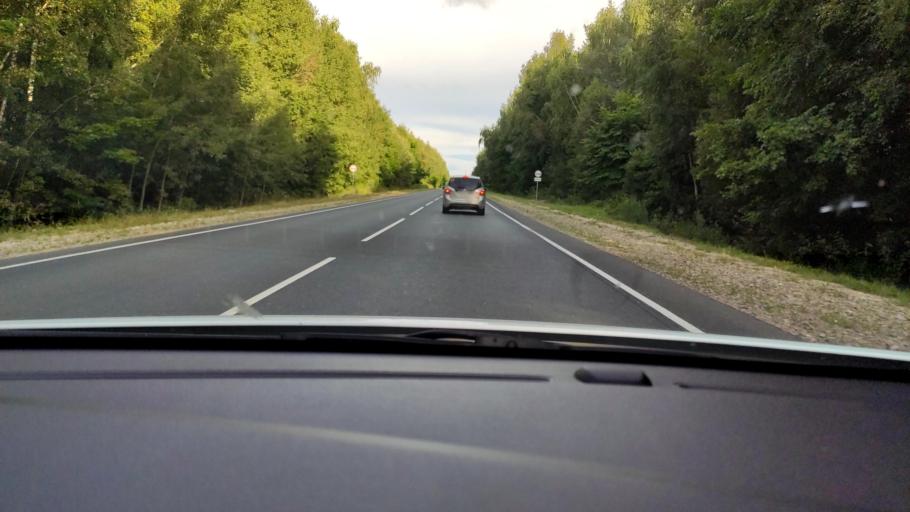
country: RU
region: Mariy-El
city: Krasnogorskiy
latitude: 56.1858
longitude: 48.2521
